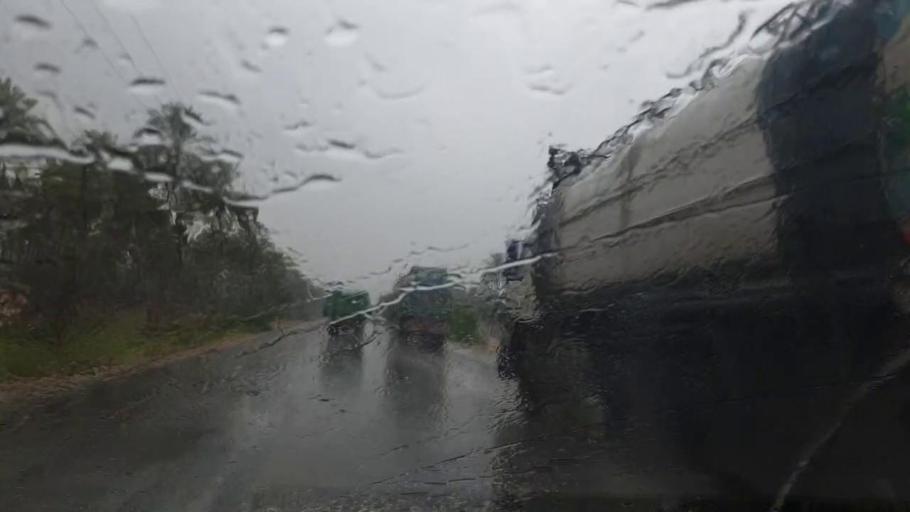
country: PK
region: Sindh
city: Khairpur
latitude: 27.5554
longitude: 68.7359
